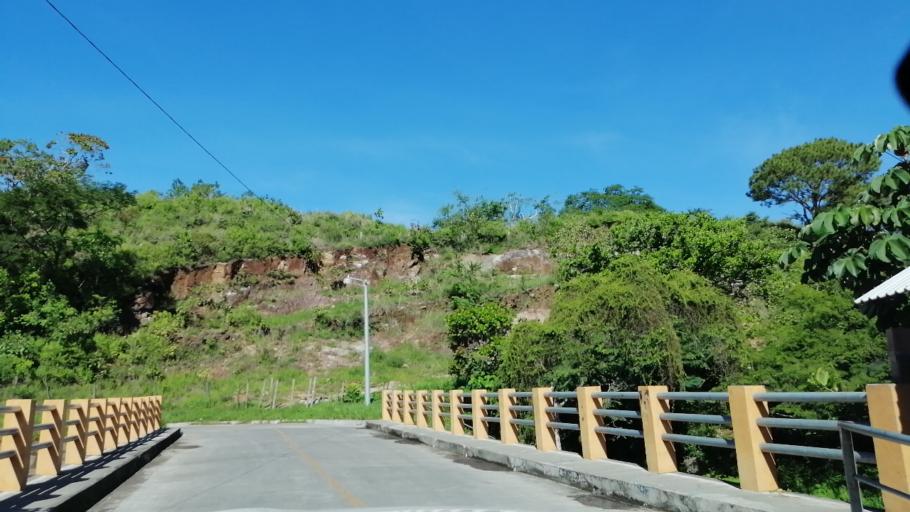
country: SV
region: Morazan
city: Corinto
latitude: 13.8081
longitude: -87.9719
